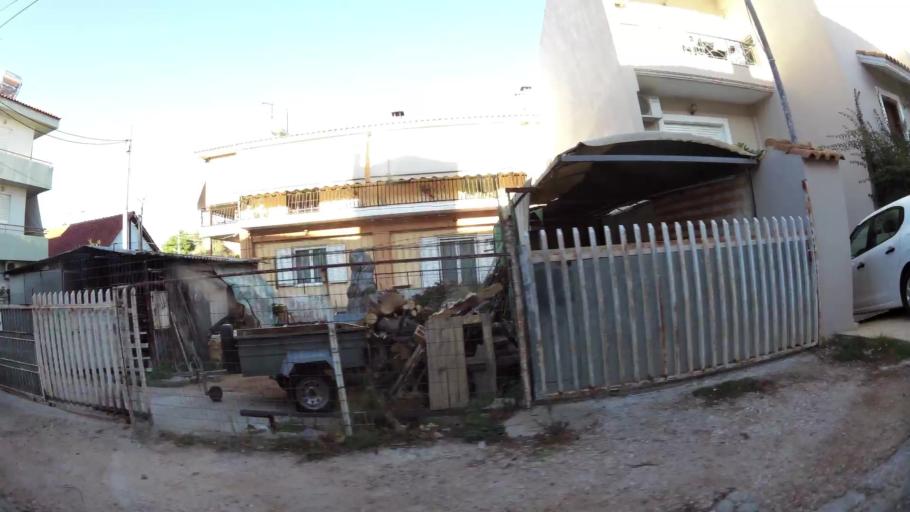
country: GR
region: Attica
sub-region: Nomarchia Athinas
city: Vrilissia
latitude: 38.0304
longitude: 23.8427
